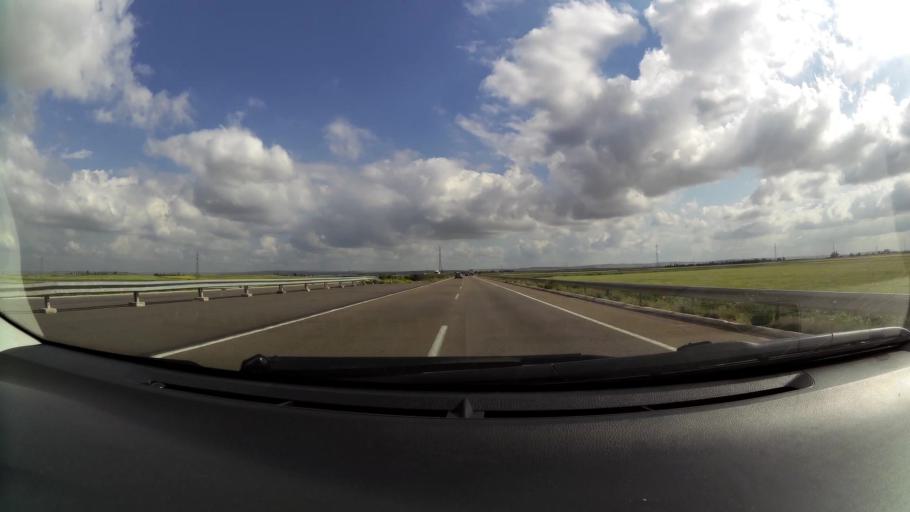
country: MA
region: Chaouia-Ouardigha
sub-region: Settat Province
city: Berrechid
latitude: 33.1763
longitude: -7.5720
